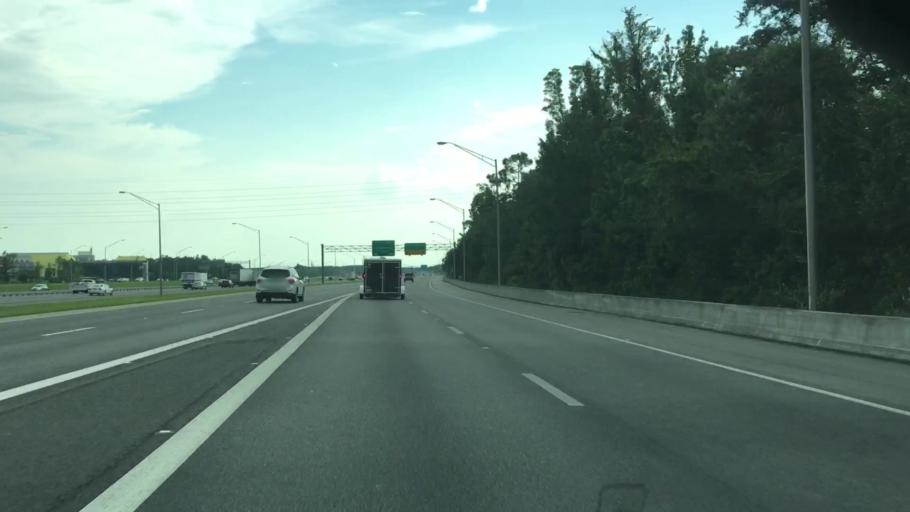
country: US
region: Florida
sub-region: Osceola County
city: Celebration
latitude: 28.3153
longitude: -81.5628
